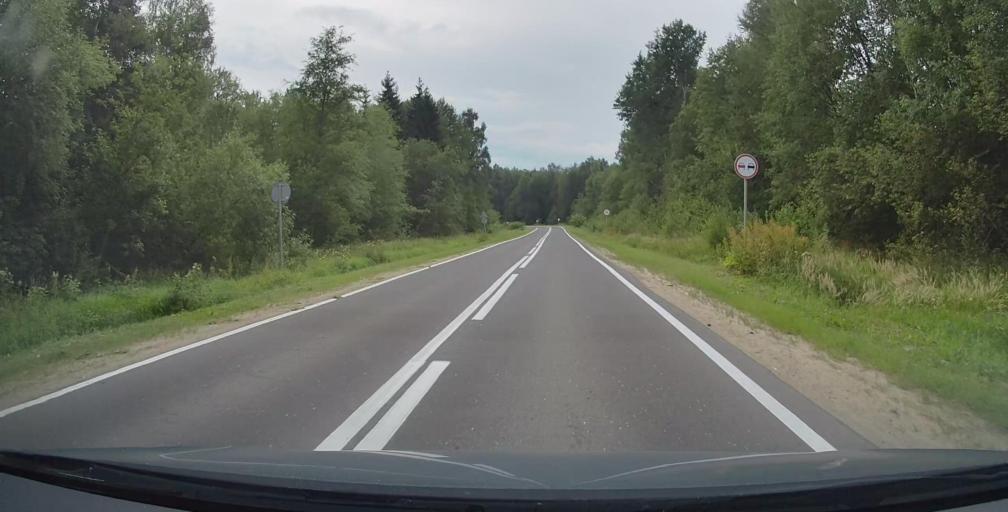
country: RU
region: Jaroslavl
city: Rybinsk
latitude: 57.9589
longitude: 38.7211
